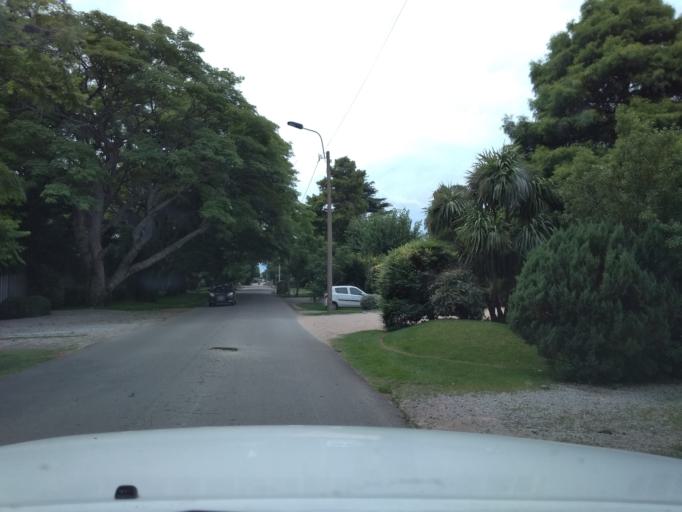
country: UY
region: Canelones
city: Paso de Carrasco
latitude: -34.8818
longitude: -56.0558
